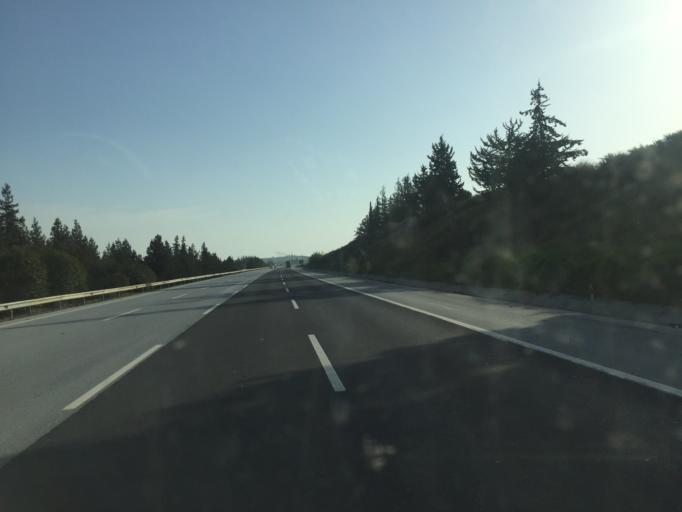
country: TR
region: Mersin
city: Yenice
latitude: 37.0227
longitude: 35.0494
